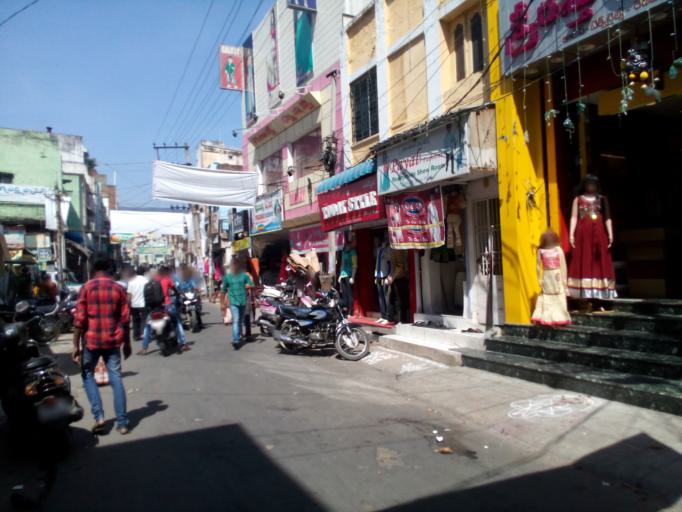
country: IN
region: Andhra Pradesh
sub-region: Chittoor
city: Tirupati
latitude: 13.6333
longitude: 79.4183
